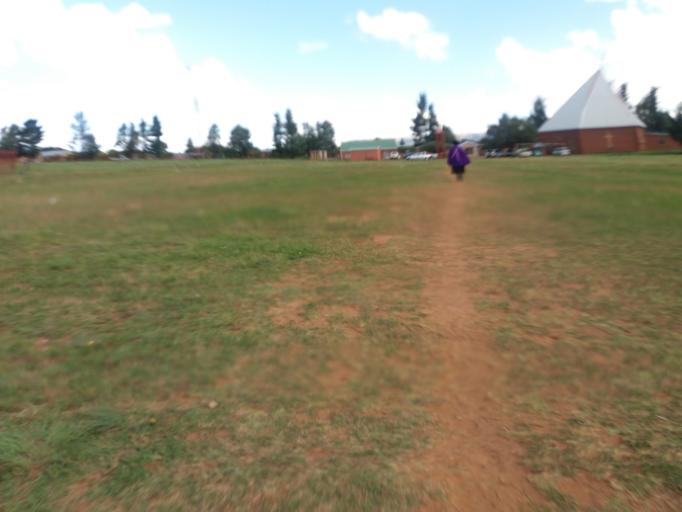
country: LS
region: Maseru
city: Maseru
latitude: -29.3706
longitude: 27.5068
